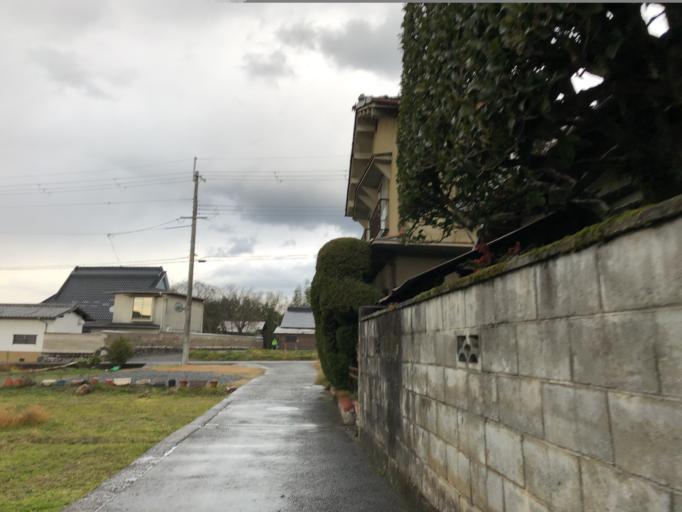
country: JP
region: Kyoto
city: Kameoka
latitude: 35.0227
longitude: 135.5946
